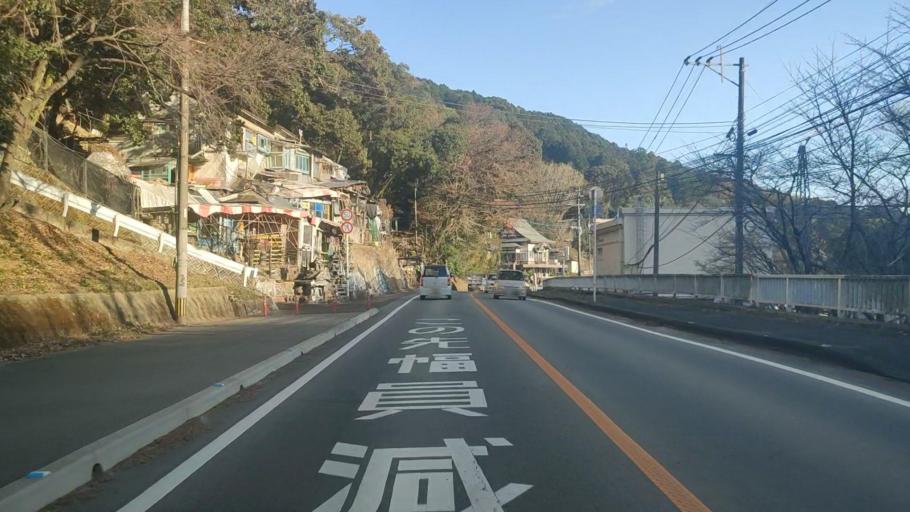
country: JP
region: Saga Prefecture
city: Saga-shi
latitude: 33.3316
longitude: 130.2655
